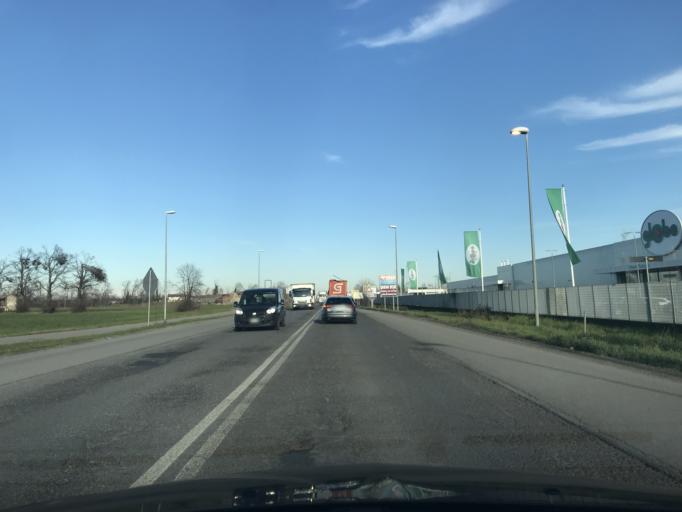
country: IT
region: Lombardy
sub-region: Provincia di Lodi
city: Muzza di Cornegliano Laudense
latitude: 45.2802
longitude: 9.4612
